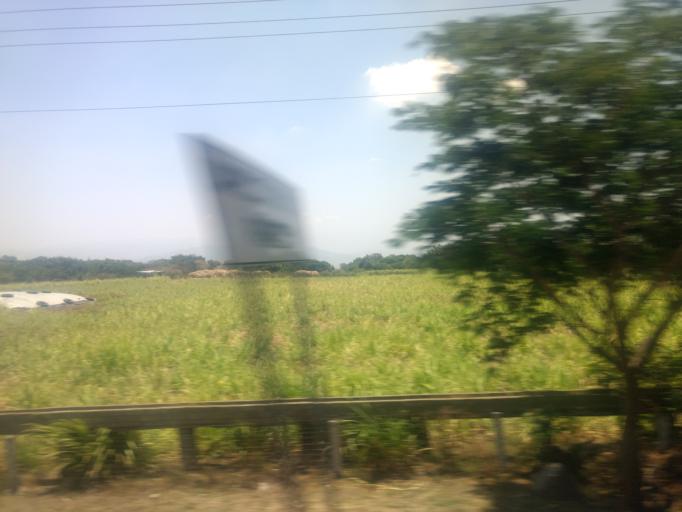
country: MX
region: Colima
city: Queseria
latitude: 19.3583
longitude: -103.5647
